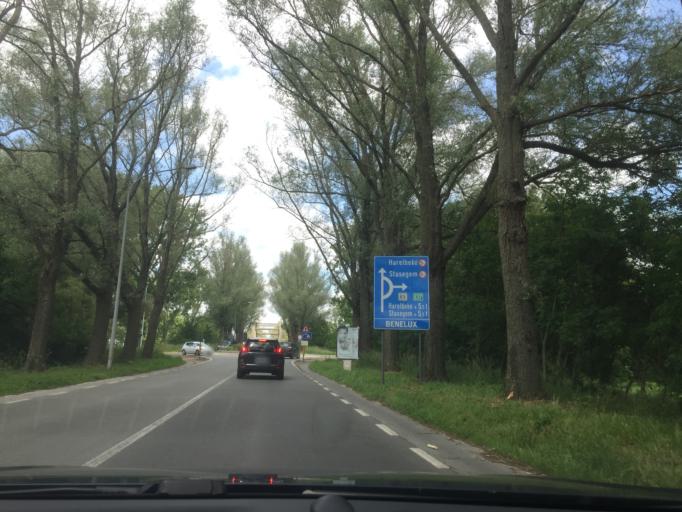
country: BE
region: Flanders
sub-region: Provincie West-Vlaanderen
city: Zwevegem
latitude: 50.8256
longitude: 3.3235
